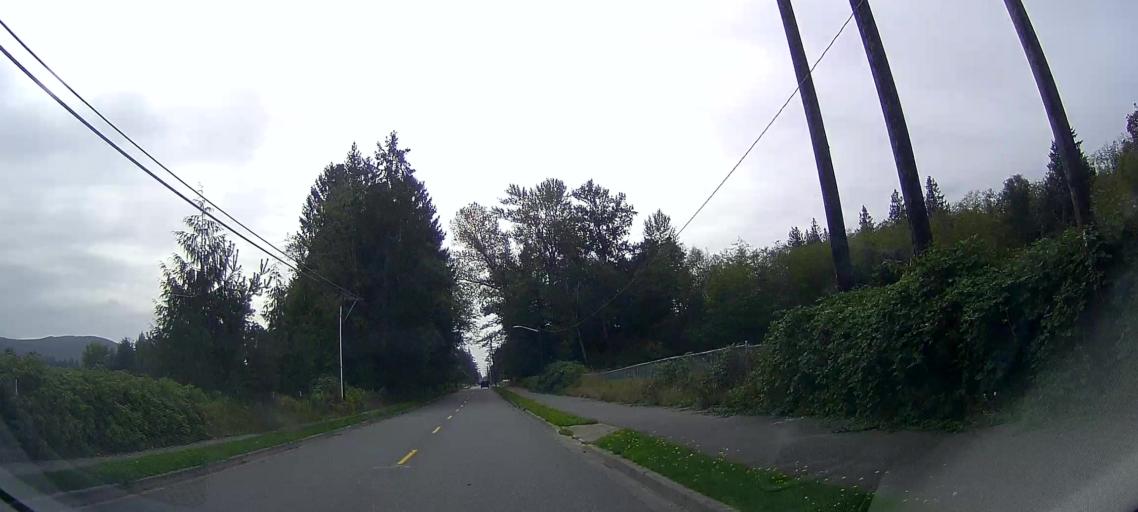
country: US
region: Washington
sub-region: Skagit County
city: Sedro-Woolley
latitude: 48.5193
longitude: -122.2150
